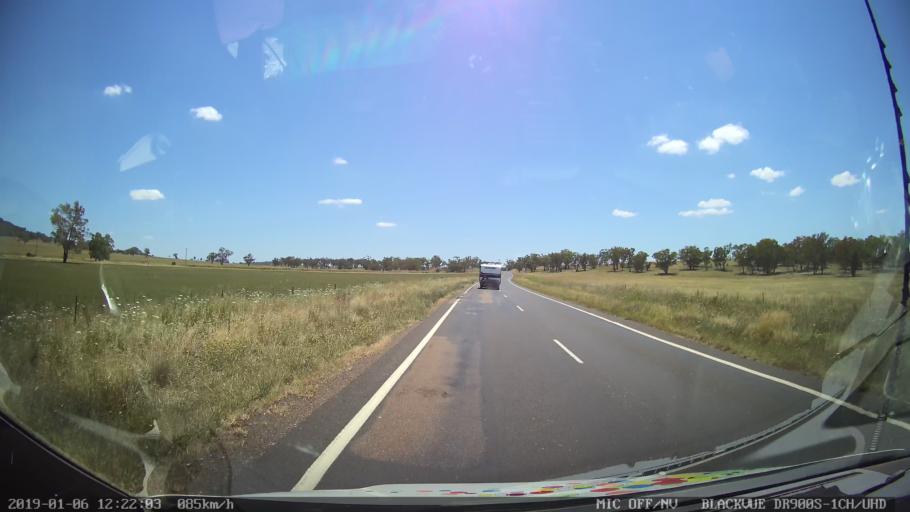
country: AU
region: New South Wales
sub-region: Tamworth Municipality
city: Phillip
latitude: -31.2662
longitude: 150.7855
